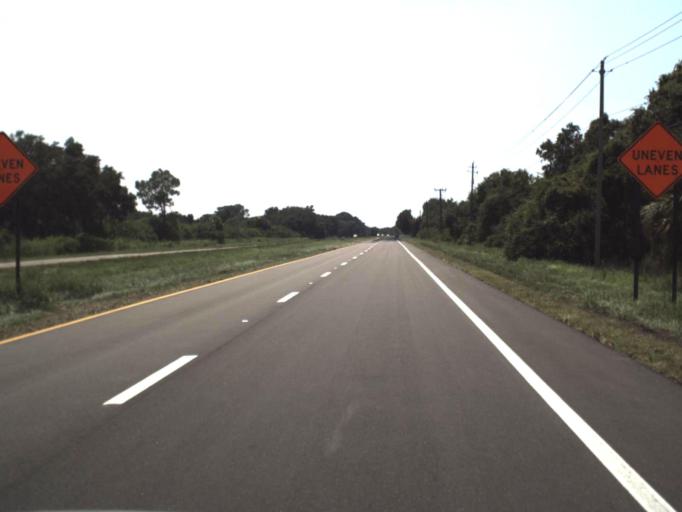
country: US
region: Florida
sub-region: Hillsborough County
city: Ruskin
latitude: 27.6574
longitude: -82.5063
